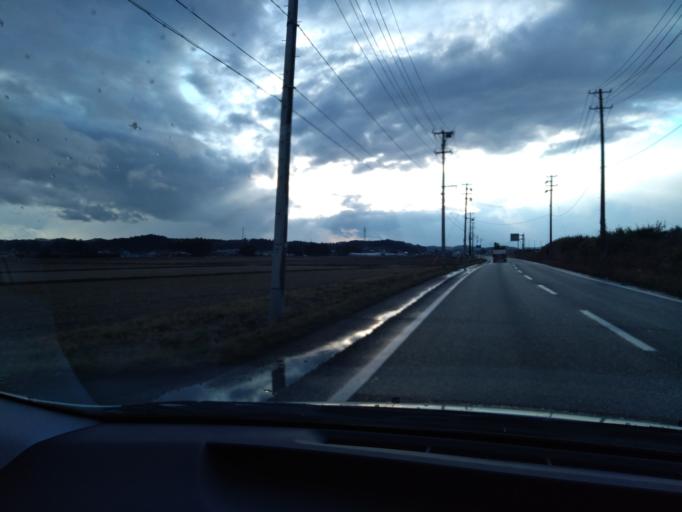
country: JP
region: Iwate
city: Ichinoseki
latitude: 38.7965
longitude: 141.0821
